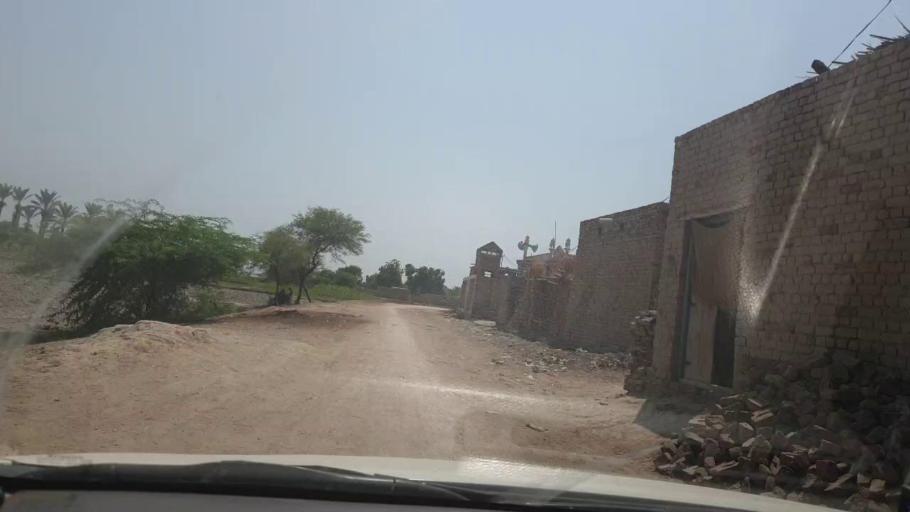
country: PK
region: Sindh
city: Lakhi
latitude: 27.8609
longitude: 68.7150
